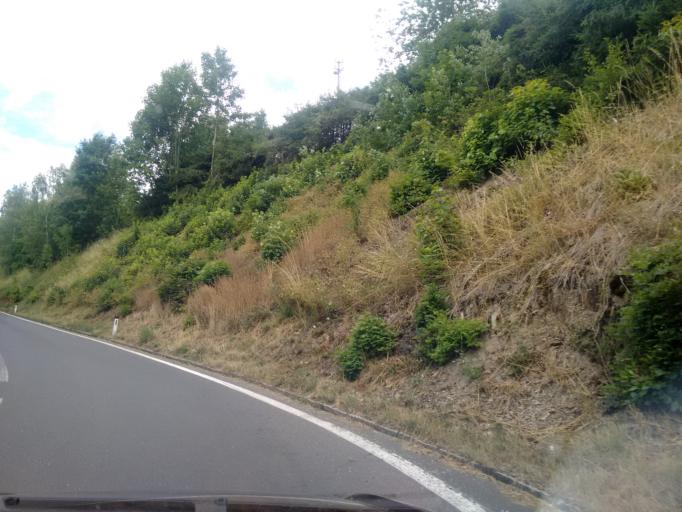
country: AT
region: Upper Austria
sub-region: Politischer Bezirk Urfahr-Umgebung
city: Gramastetten
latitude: 48.3854
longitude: 14.1950
